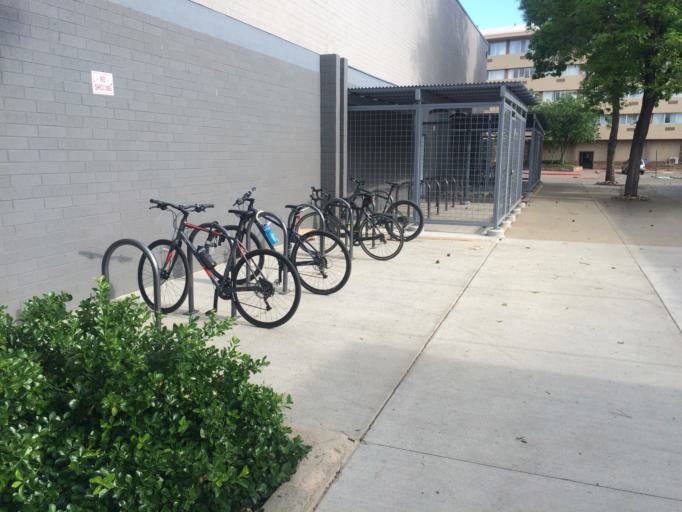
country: US
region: Colorado
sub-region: Boulder County
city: Boulder
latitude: 40.0135
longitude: -105.2602
